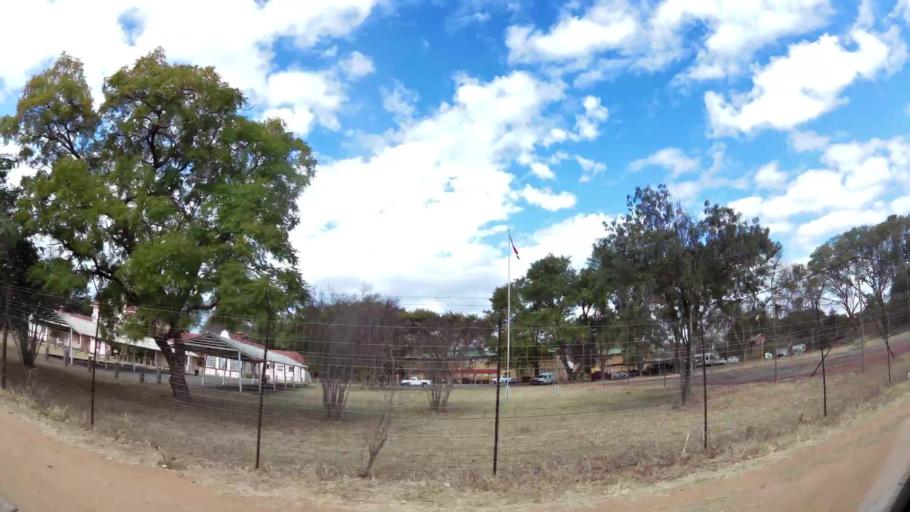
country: ZA
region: Limpopo
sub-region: Waterberg District Municipality
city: Modimolle
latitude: -24.7042
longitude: 28.4010
